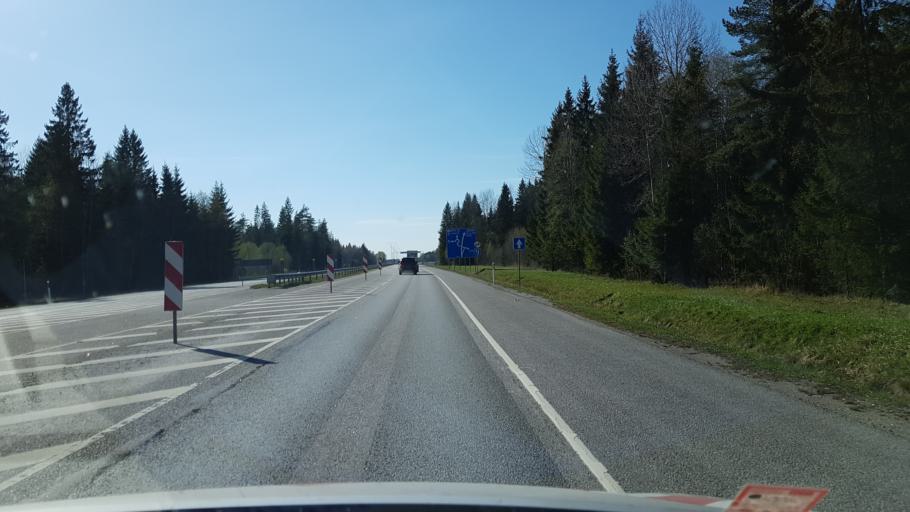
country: EE
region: Jaervamaa
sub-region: Paide linn
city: Paide
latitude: 58.8960
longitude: 25.6580
